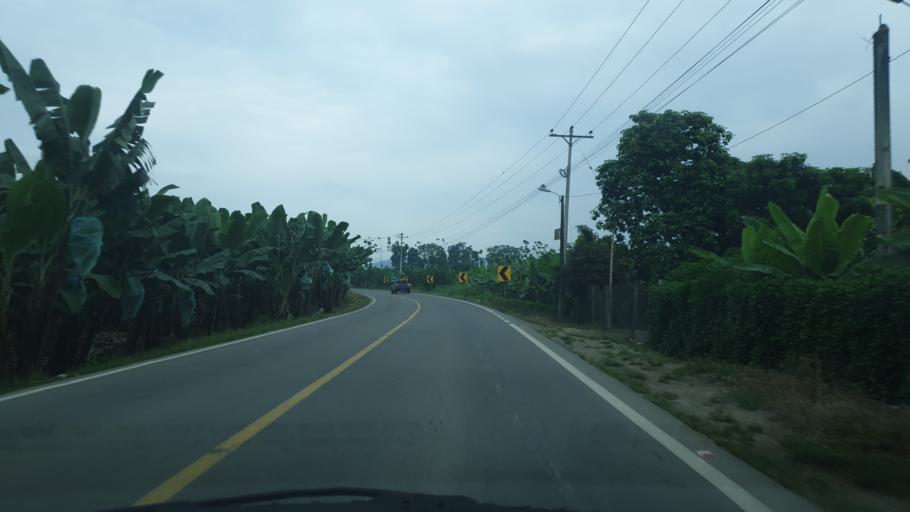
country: EC
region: El Oro
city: Pasaje
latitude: -3.3540
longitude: -79.8187
